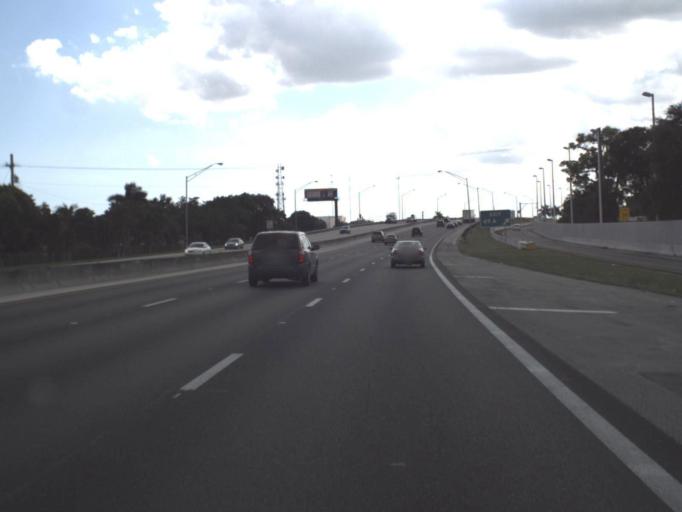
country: US
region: Florida
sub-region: Broward County
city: Pembroke Pines
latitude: 26.0146
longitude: -80.2128
